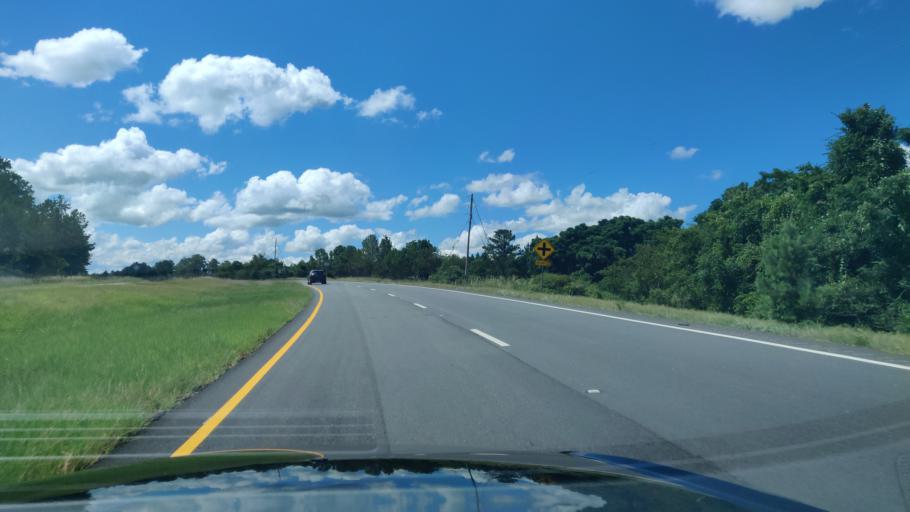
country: US
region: Georgia
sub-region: Stewart County
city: Richland
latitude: 32.1596
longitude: -84.6985
